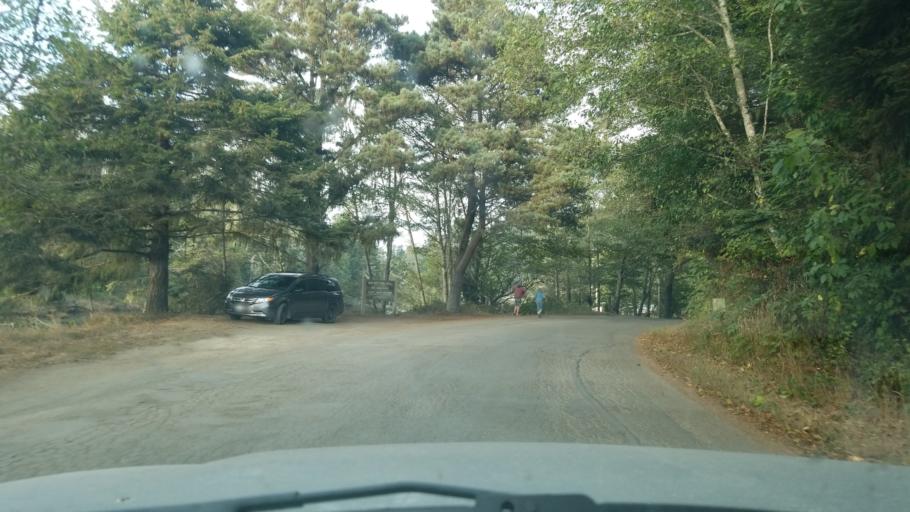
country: US
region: California
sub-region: Mendocino County
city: Fort Bragg
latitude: 39.4261
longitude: -123.7994
